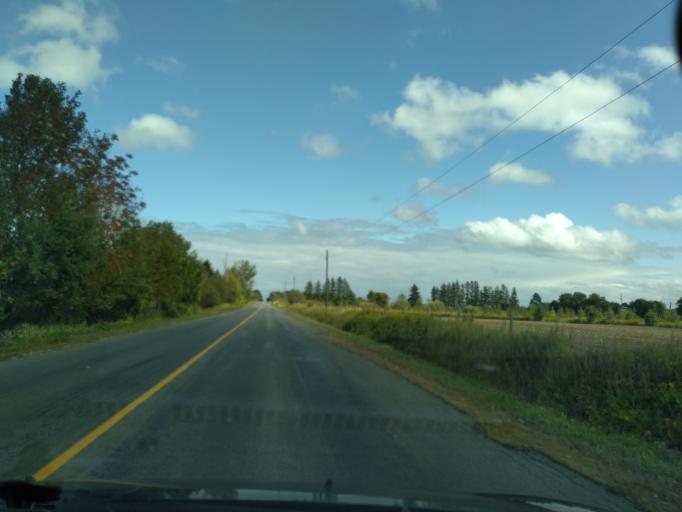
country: CA
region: Ontario
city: Innisfil
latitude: 44.2815
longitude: -79.5841
